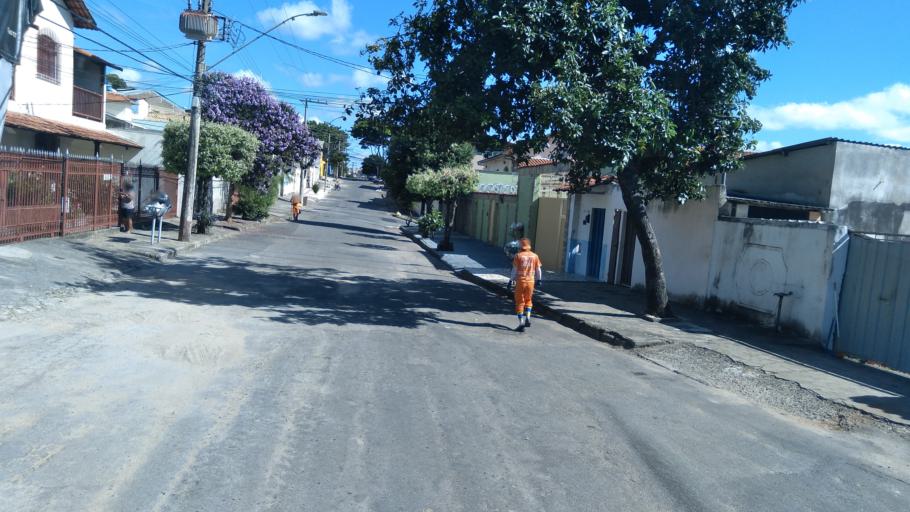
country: BR
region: Minas Gerais
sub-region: Belo Horizonte
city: Belo Horizonte
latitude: -19.8554
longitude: -43.9141
